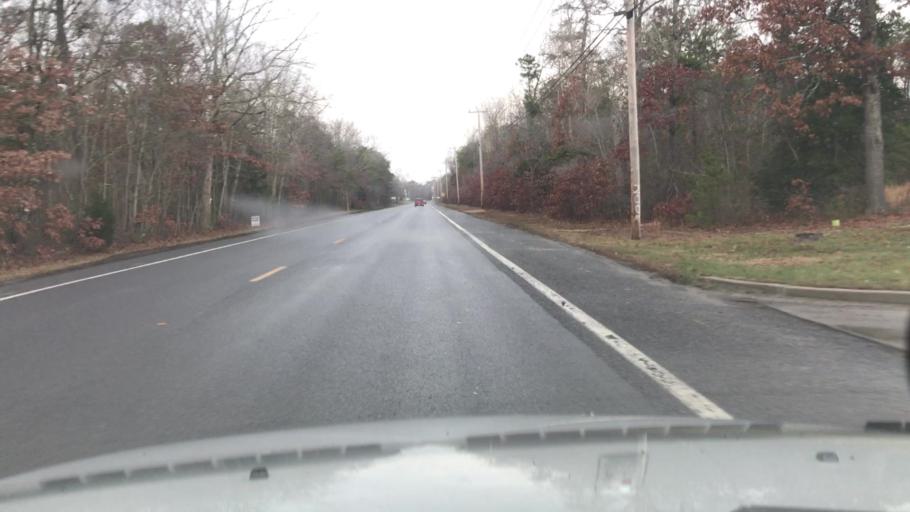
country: US
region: New Jersey
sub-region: Cape May County
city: Sea Isle City
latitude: 39.1981
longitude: -74.7512
